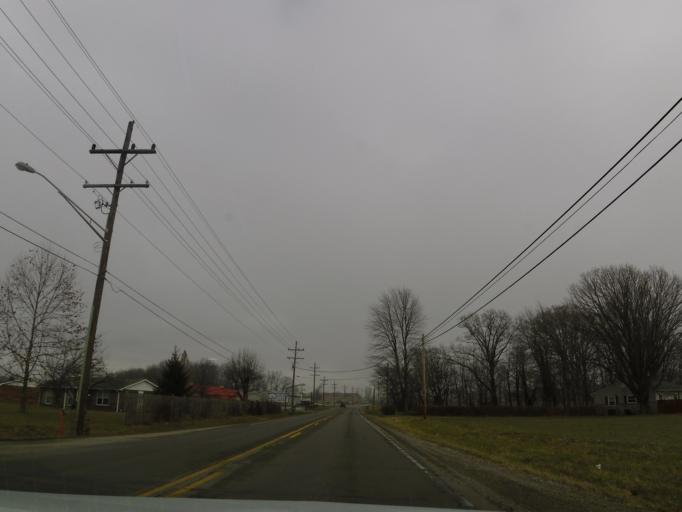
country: US
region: Indiana
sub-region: Jefferson County
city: Hanover
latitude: 38.7327
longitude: -85.4533
